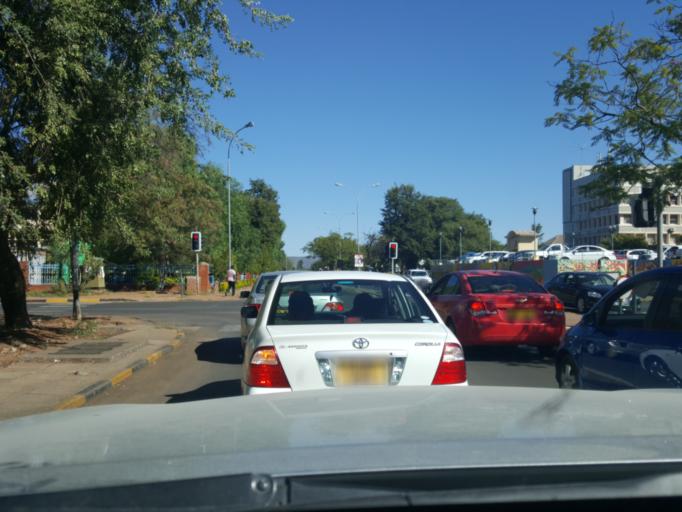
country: BW
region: South East
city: Gaborone
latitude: -24.6573
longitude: 25.9191
